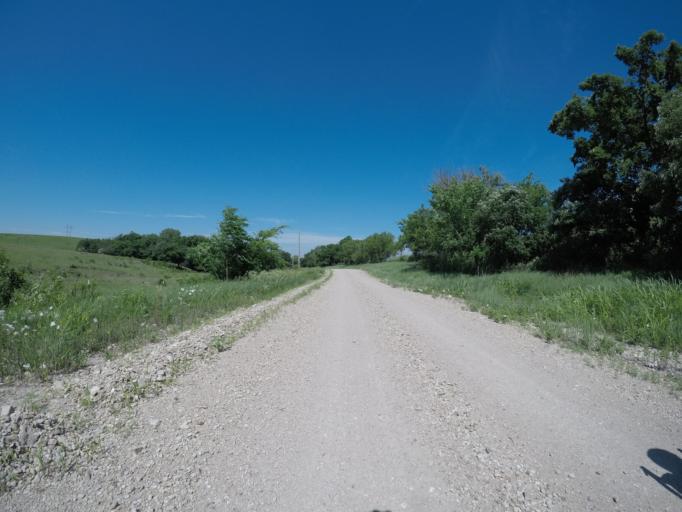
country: US
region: Kansas
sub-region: Wabaunsee County
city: Alma
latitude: 39.0005
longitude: -96.1867
